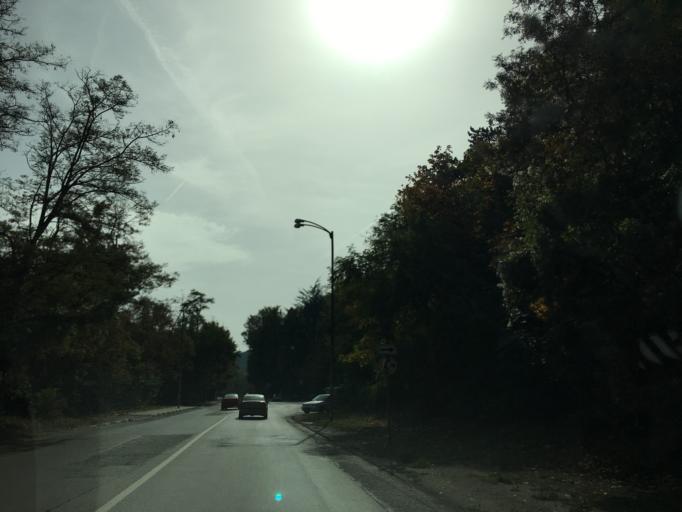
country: BG
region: Sofia-Capital
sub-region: Stolichna Obshtina
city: Sofia
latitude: 42.6040
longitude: 23.4019
